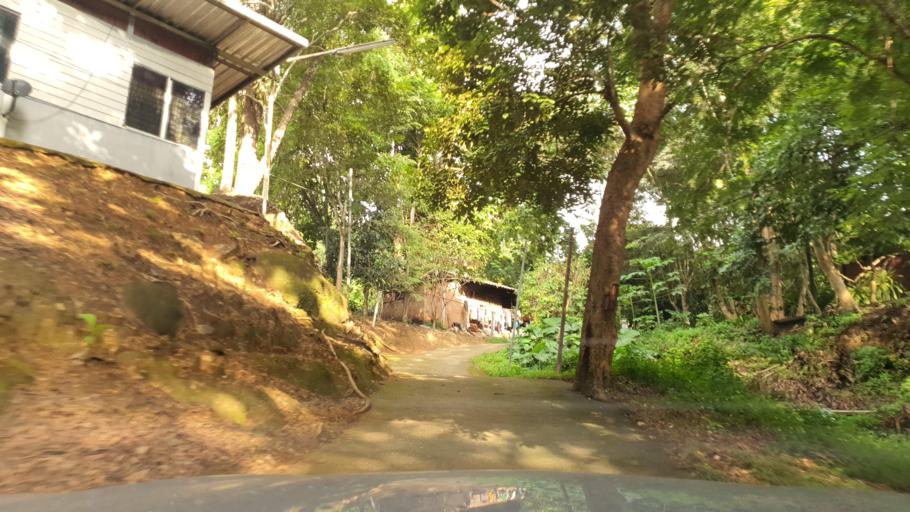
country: TH
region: Chiang Mai
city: Mae On
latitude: 18.9759
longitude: 99.2560
